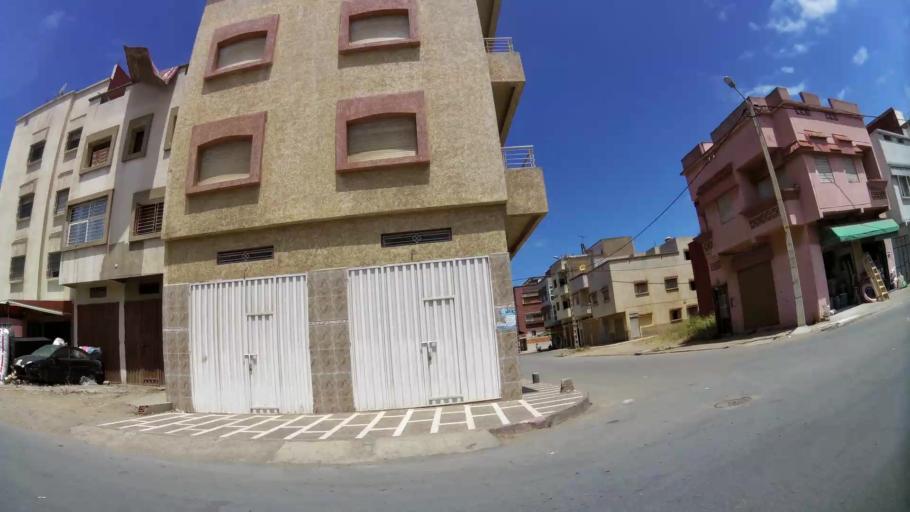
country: MA
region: Gharb-Chrarda-Beni Hssen
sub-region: Kenitra Province
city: Kenitra
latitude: 34.2668
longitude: -6.6050
